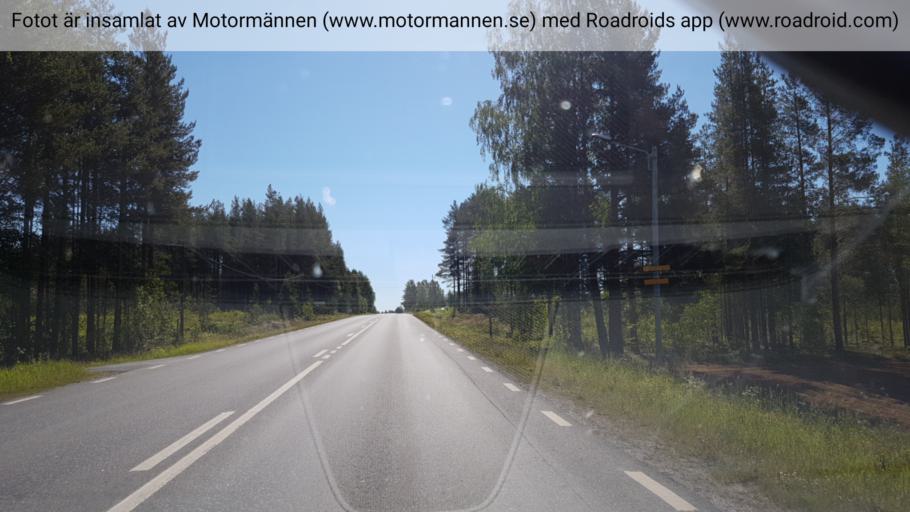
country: SE
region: Norrbotten
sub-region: Bodens Kommun
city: Boden
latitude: 65.8573
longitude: 21.4697
